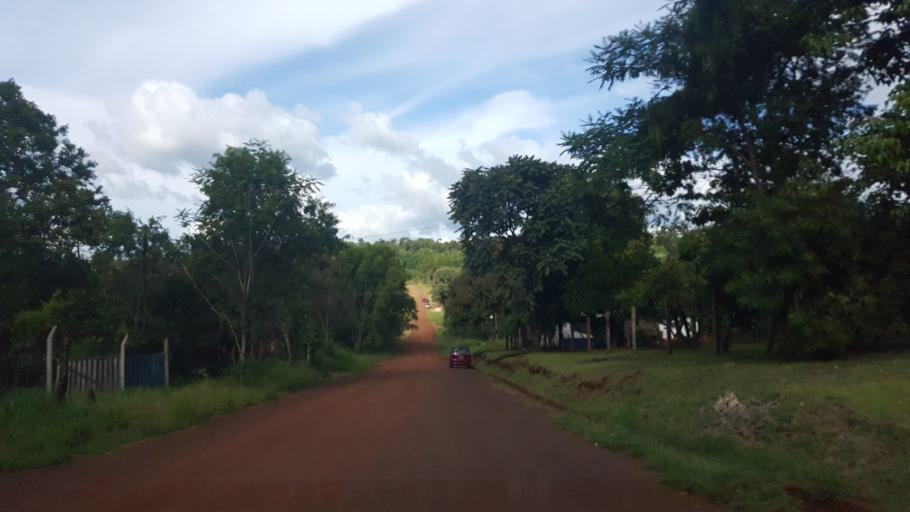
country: AR
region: Misiones
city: Santa Ana
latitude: -27.3675
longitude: -55.5765
